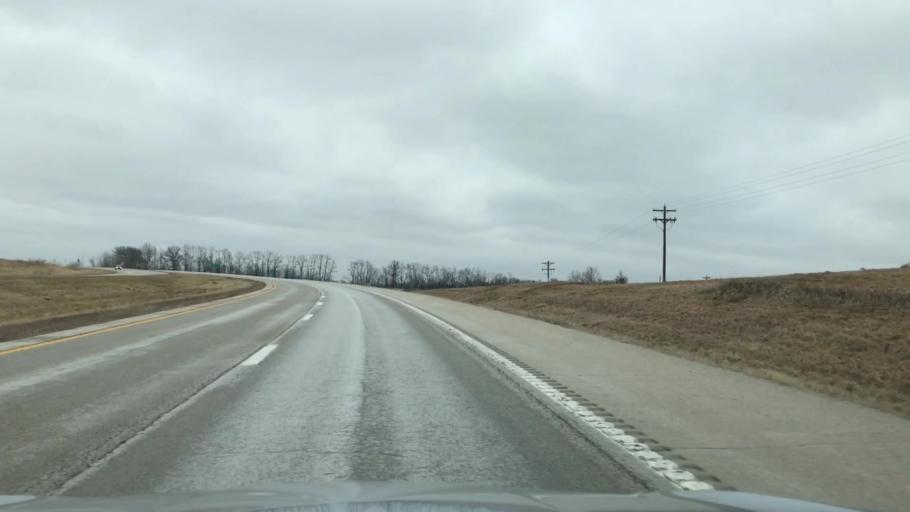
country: US
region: Missouri
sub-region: Livingston County
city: Chillicothe
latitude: 39.7372
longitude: -93.6342
